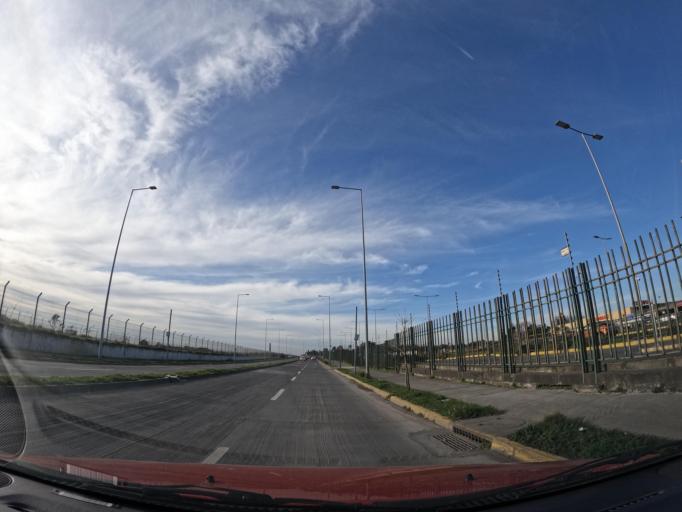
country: CL
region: Biobio
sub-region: Provincia de Concepcion
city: Concepcion
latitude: -36.7895
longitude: -73.0688
